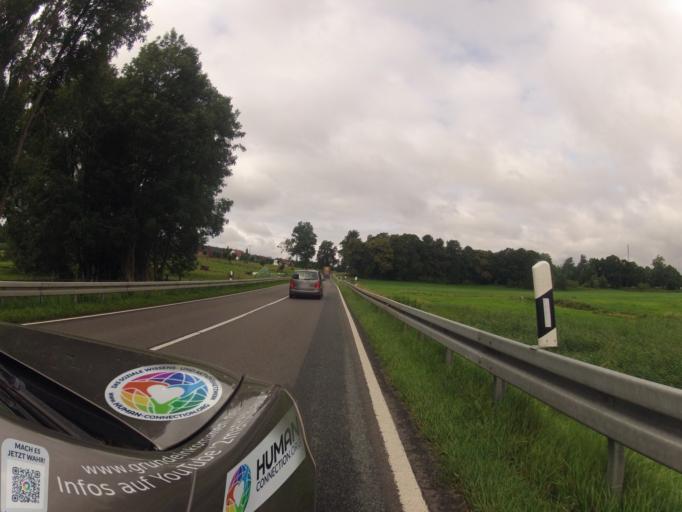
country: DE
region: Mecklenburg-Vorpommern
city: Lassan
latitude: 53.9040
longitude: 13.7768
